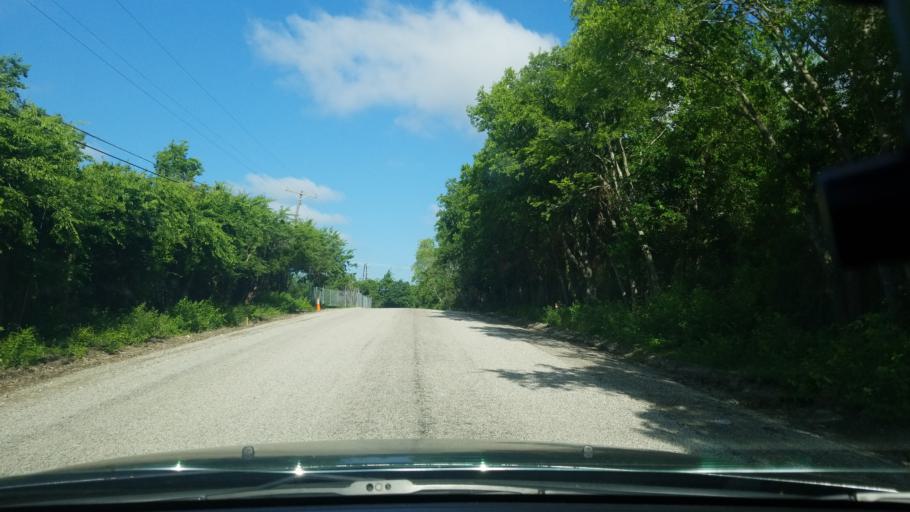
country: US
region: Texas
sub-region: Dallas County
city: Sunnyvale
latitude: 32.8045
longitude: -96.5588
